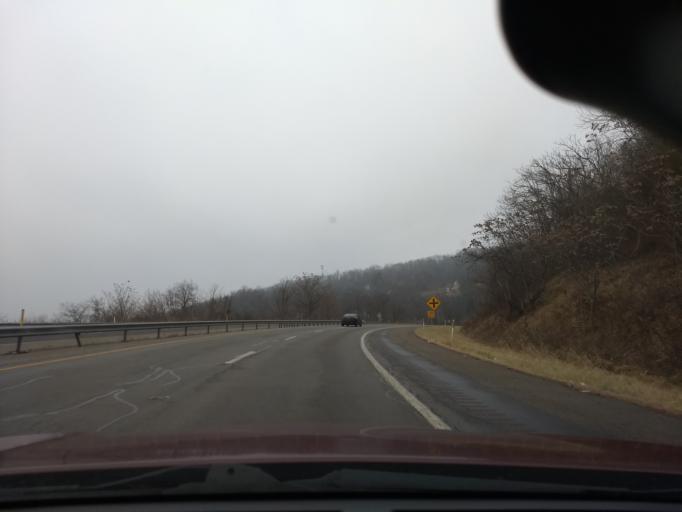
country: US
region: Pennsylvania
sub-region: Allegheny County
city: East Pittsburgh
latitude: 40.3952
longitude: -79.8316
